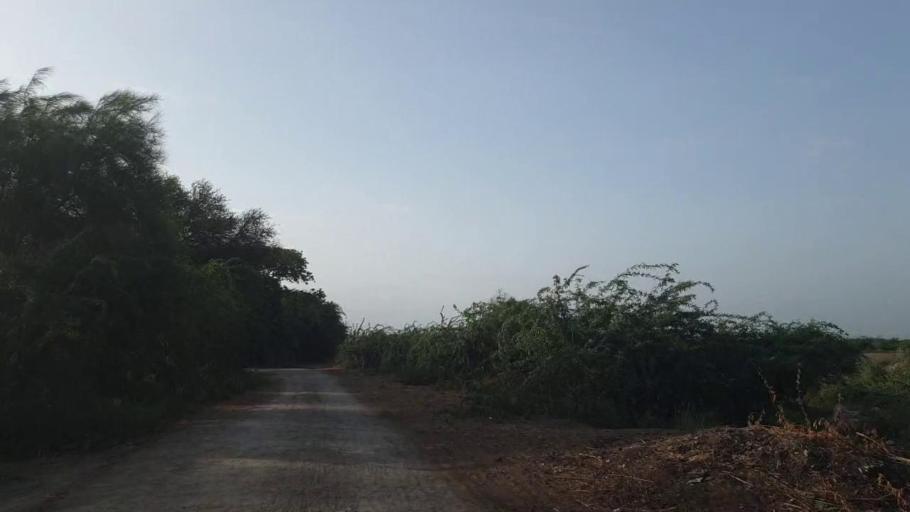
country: PK
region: Sindh
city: Kadhan
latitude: 24.6347
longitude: 69.1578
